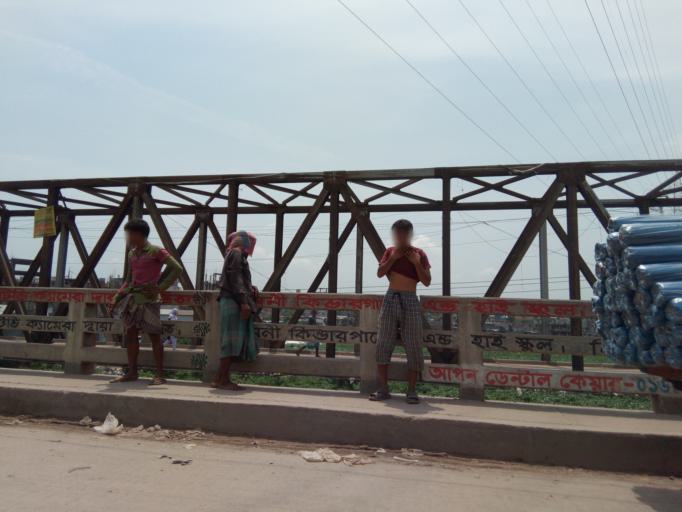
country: BD
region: Dhaka
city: Azimpur
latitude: 23.7139
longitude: 90.3813
